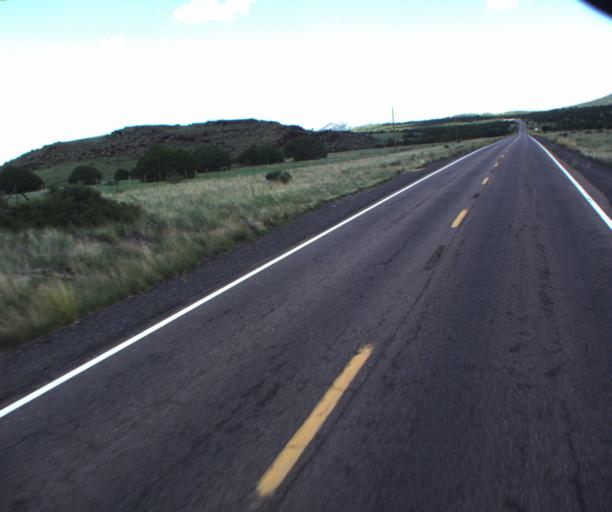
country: US
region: Arizona
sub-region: Navajo County
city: Pinetop-Lakeside
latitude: 34.2693
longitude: -109.6305
